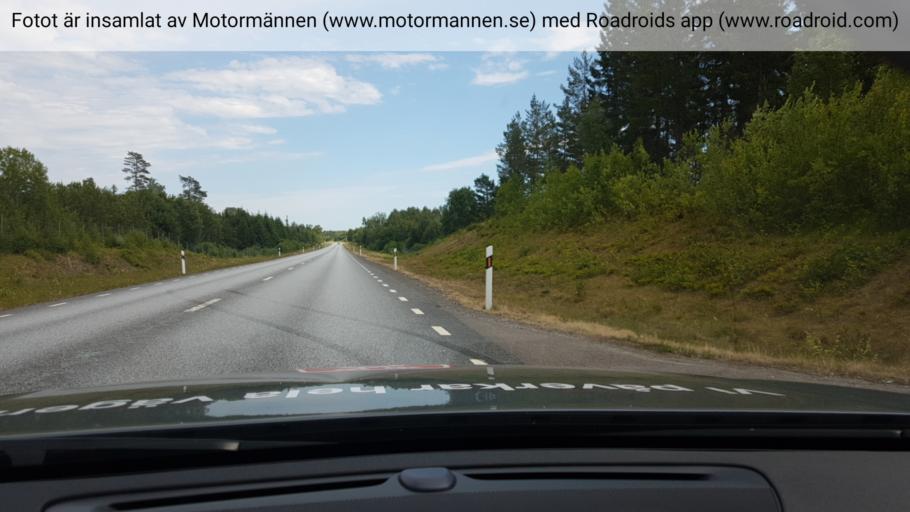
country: SE
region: Uppsala
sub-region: Osthammars Kommun
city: OEsthammar
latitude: 60.1726
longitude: 18.3100
